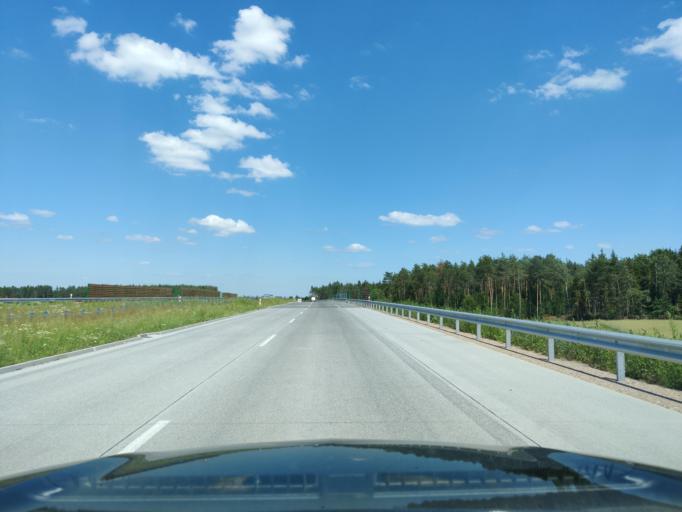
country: PL
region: Masovian Voivodeship
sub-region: Powiat mlawski
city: Wisniewo
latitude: 52.9789
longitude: 20.3354
